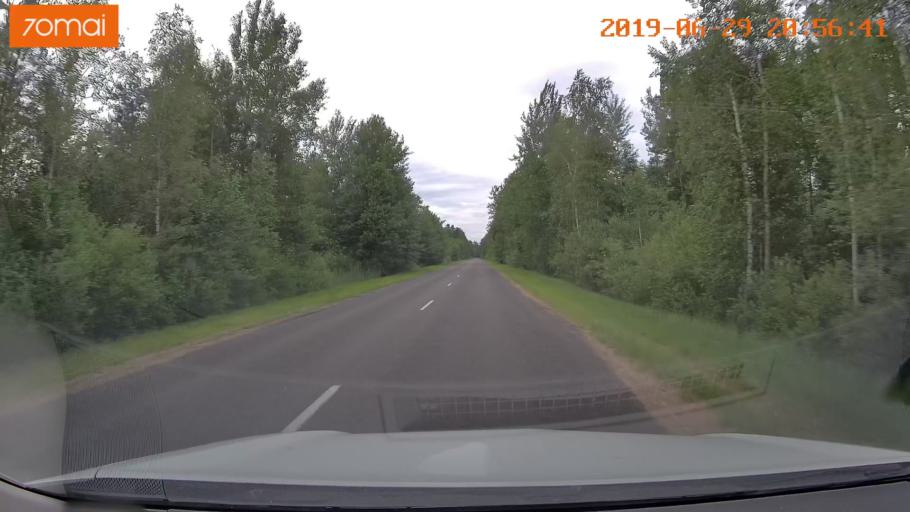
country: BY
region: Brest
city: Hantsavichy
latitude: 52.7086
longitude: 26.3686
